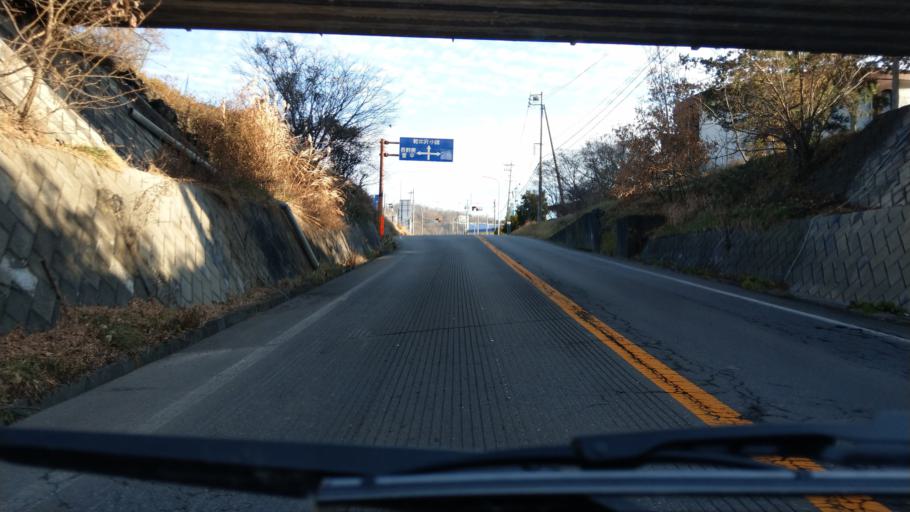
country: JP
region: Nagano
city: Ueda
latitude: 36.3938
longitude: 138.3002
